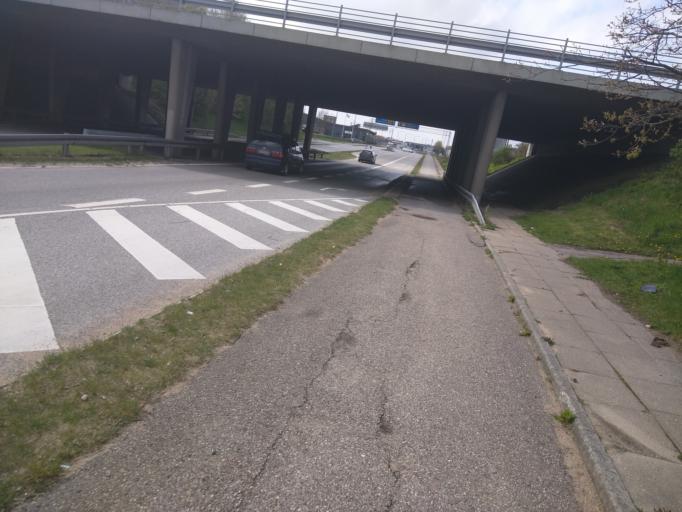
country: DK
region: Central Jutland
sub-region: Viborg Kommune
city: Viborg
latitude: 56.4682
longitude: 9.4141
